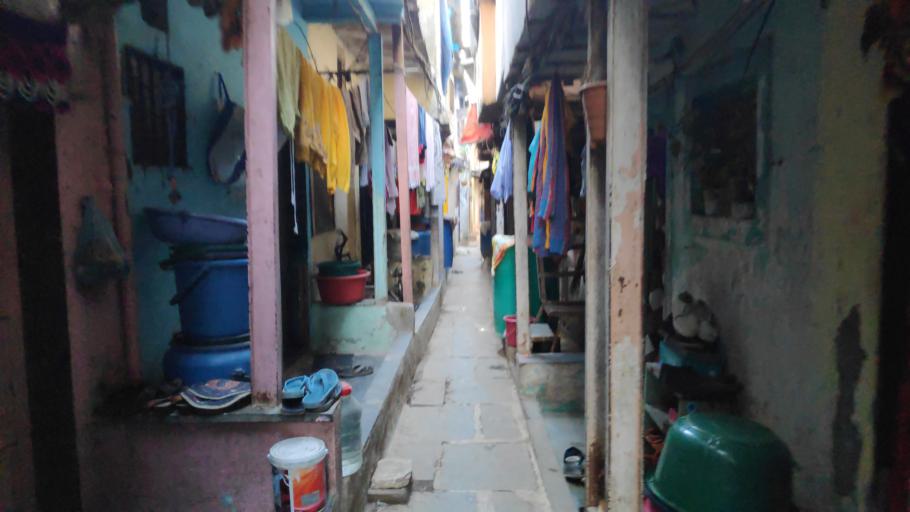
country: IN
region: Maharashtra
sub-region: Mumbai Suburban
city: Mumbai
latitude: 19.0758
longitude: 72.8482
